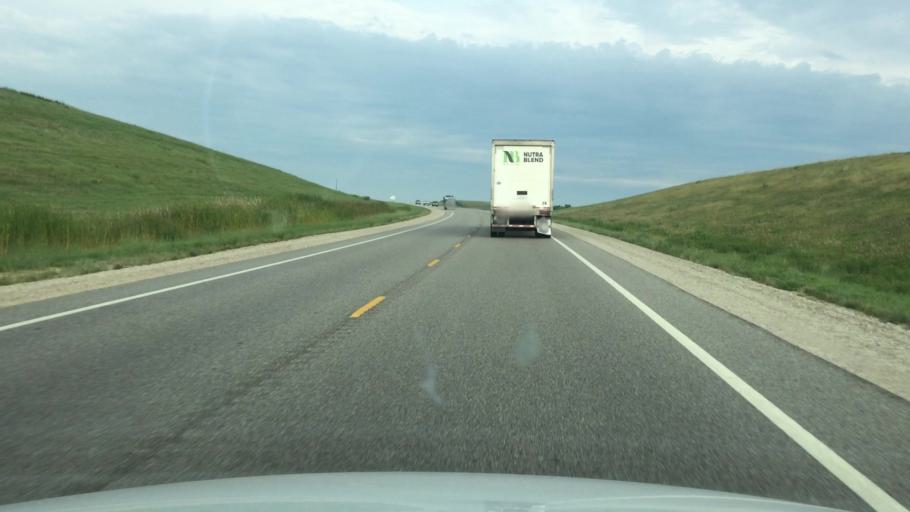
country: US
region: Kansas
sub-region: Doniphan County
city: Highland
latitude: 39.8419
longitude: -95.2768
